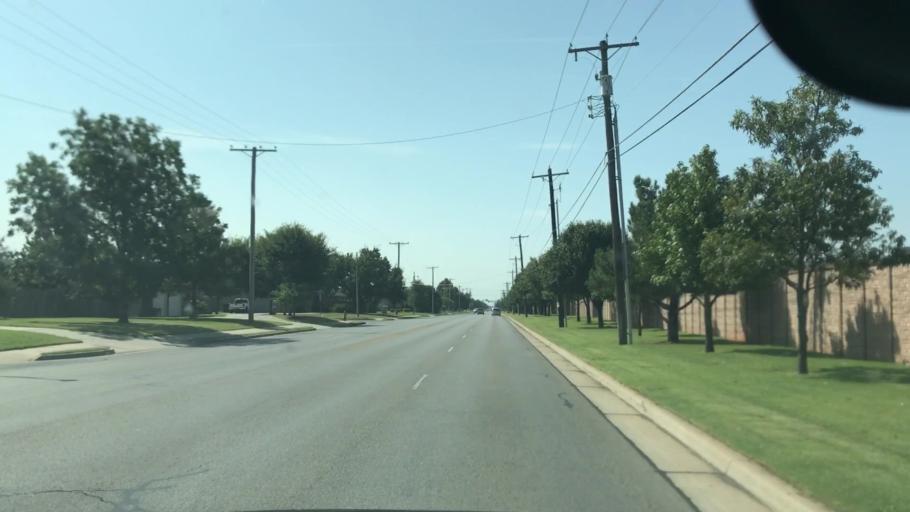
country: US
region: Oklahoma
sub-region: Cleveland County
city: Moore
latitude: 35.3543
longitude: -97.5122
